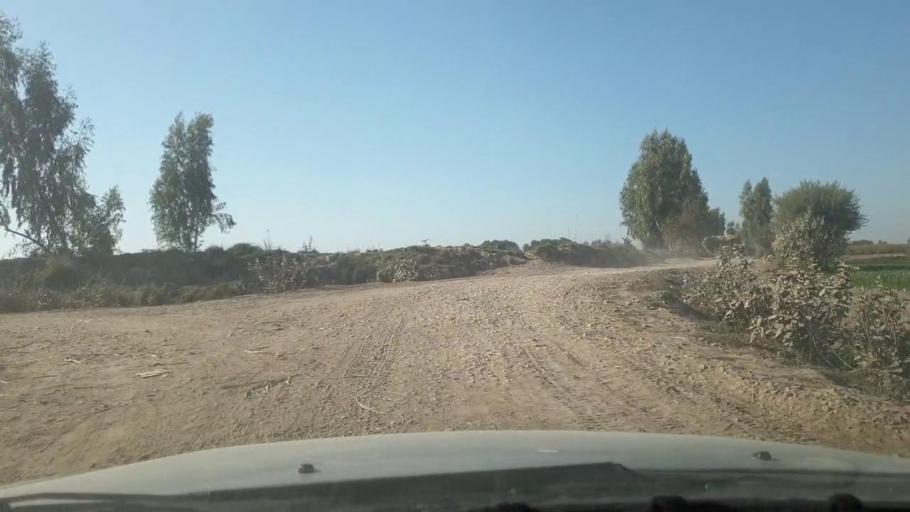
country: PK
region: Sindh
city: Pano Aqil
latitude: 27.9733
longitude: 69.1746
